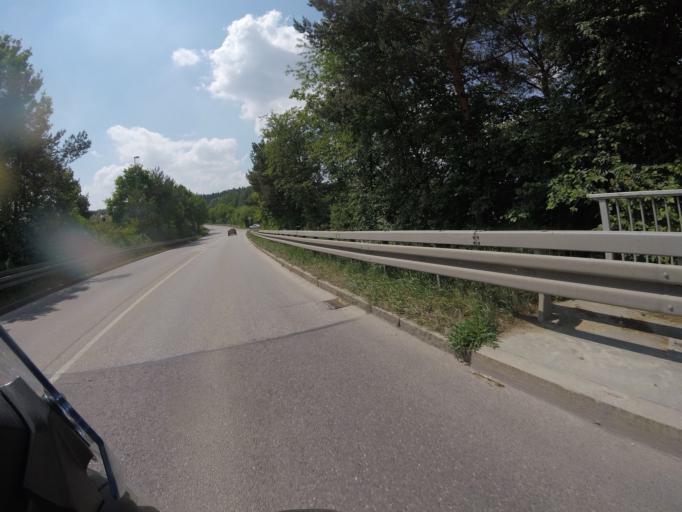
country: DE
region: Bavaria
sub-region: Upper Bavaria
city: Pfaffenhofen an der Ilm
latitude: 48.5366
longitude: 11.4869
